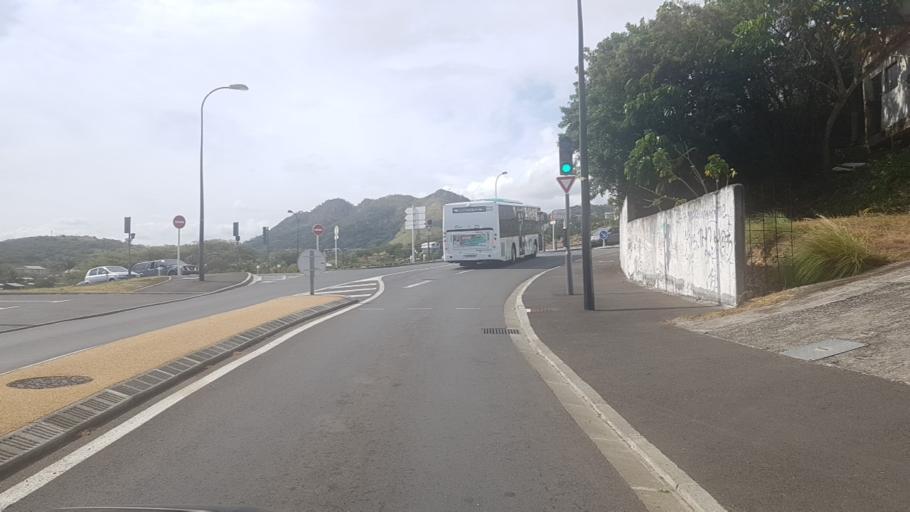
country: NC
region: South Province
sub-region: Dumbea
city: Dumbea
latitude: -22.2117
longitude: 166.4667
